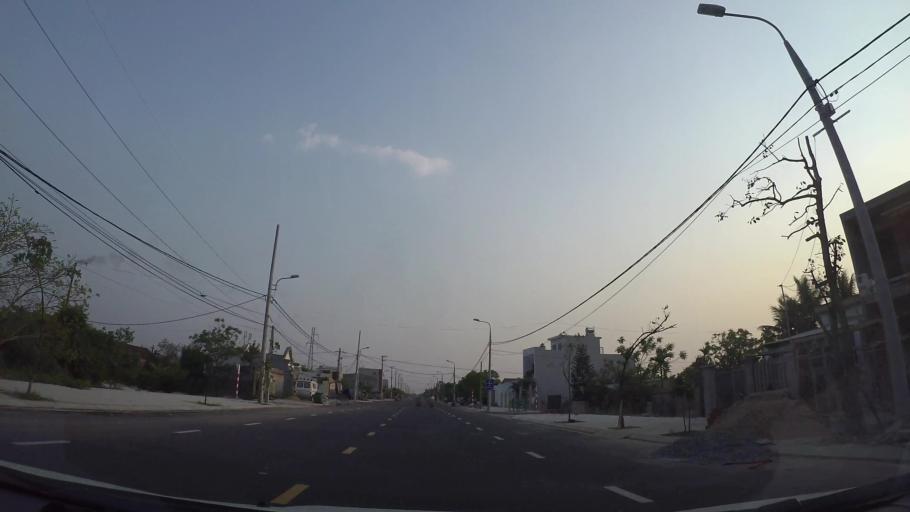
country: VN
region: Da Nang
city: Ngu Hanh Son
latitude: 15.9705
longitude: 108.2317
